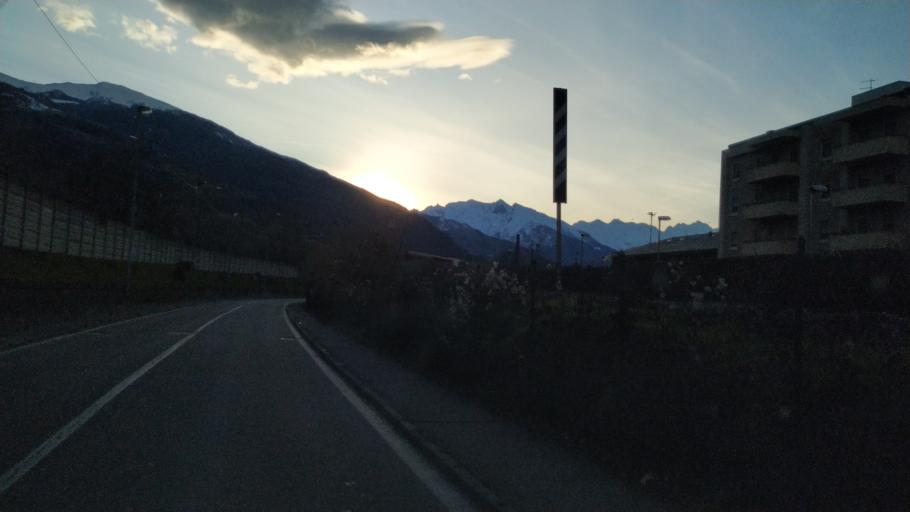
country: IT
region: Aosta Valley
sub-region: Valle d'Aosta
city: Pollein
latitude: 45.7376
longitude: 7.3364
